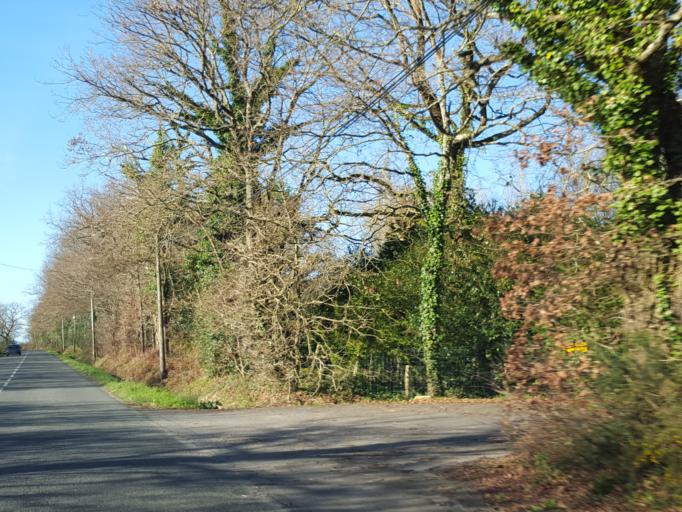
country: FR
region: Pays de la Loire
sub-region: Departement de la Vendee
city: Venansault
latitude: 46.6823
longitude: -1.4987
